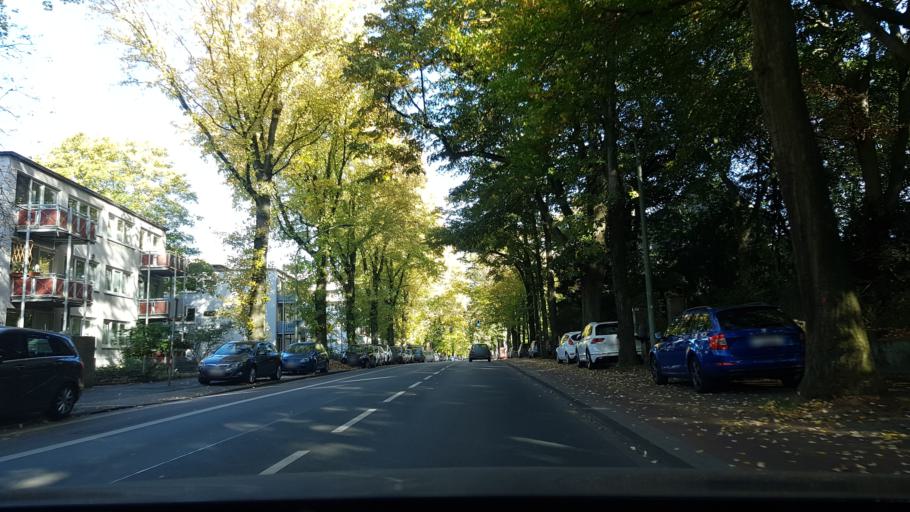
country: DE
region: North Rhine-Westphalia
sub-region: Regierungsbezirk Dusseldorf
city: Duisburg
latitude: 51.4365
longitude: 6.7961
